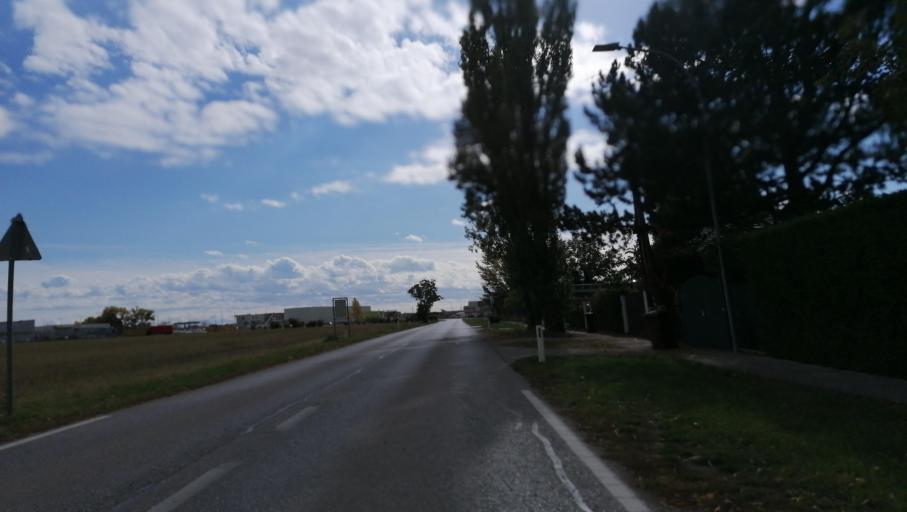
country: AT
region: Lower Austria
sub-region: Politischer Bezirk Baden
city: Teesdorf
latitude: 47.9779
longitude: 16.2779
